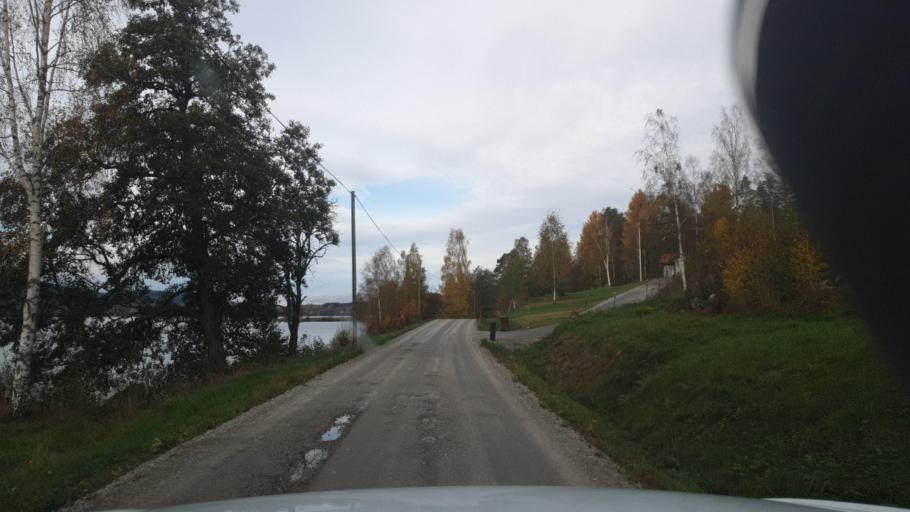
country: SE
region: Vaermland
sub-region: Arvika Kommun
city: Arvika
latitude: 59.7236
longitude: 12.8369
